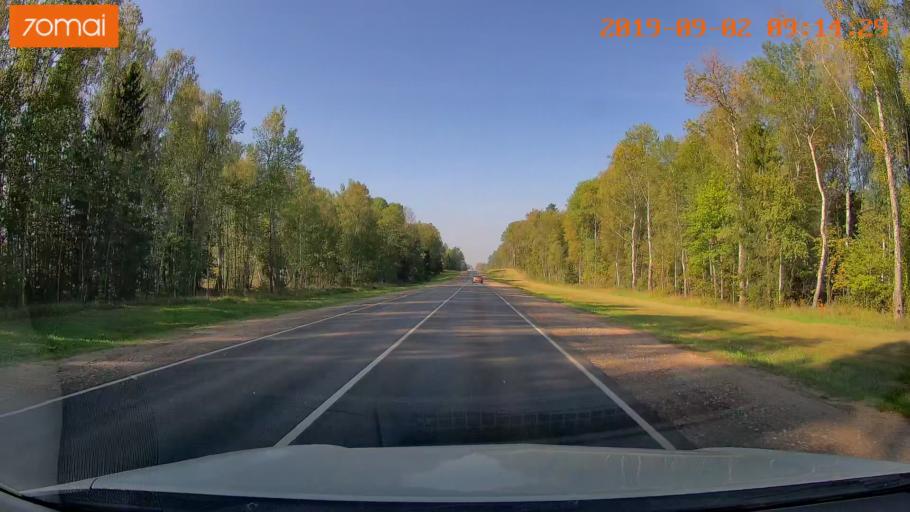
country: RU
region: Kaluga
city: Nikola-Lenivets
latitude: 54.8461
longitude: 35.5142
